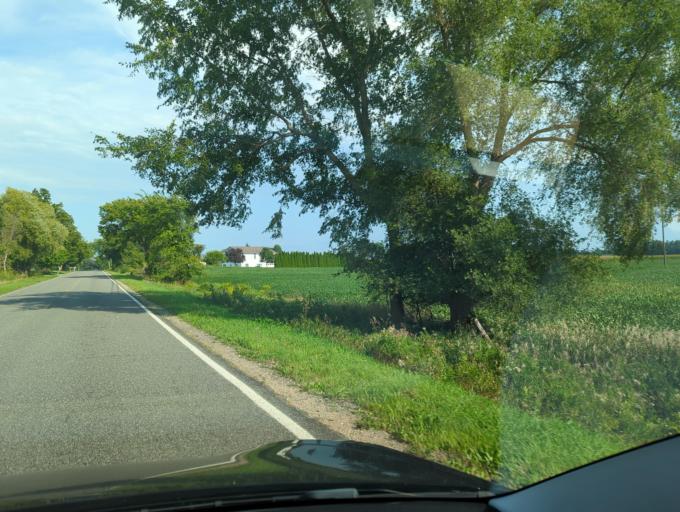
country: US
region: Michigan
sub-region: Ionia County
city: Ionia
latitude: 42.9297
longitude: -85.0915
